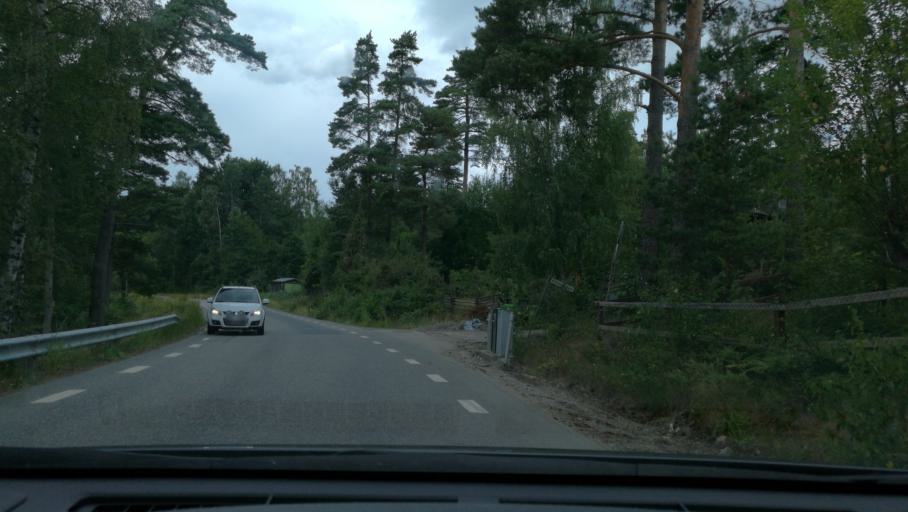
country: SE
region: OEstergoetland
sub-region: Norrkopings Kommun
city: Krokek
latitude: 58.6662
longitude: 16.3544
